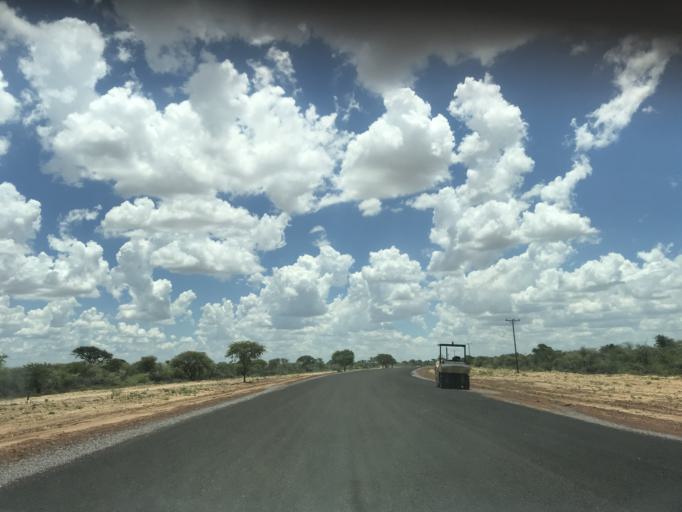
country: BW
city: Mabuli
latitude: -25.8006
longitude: 24.6702
